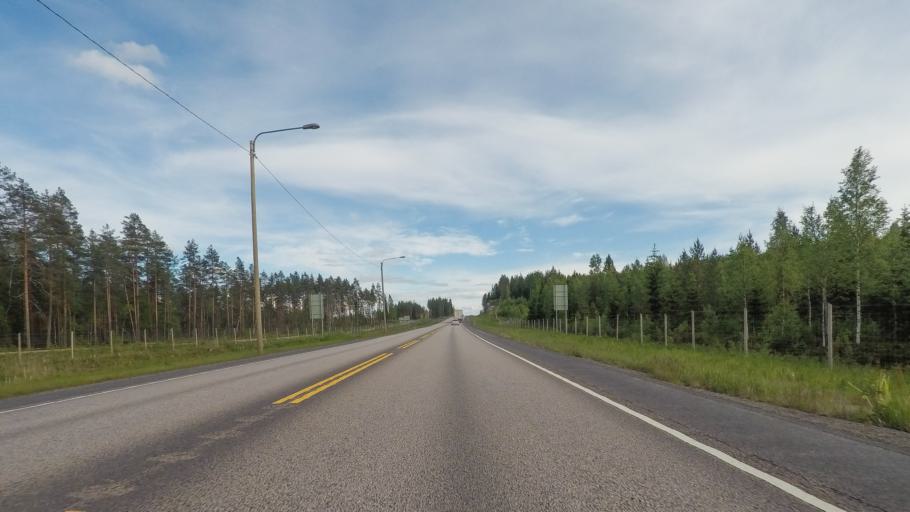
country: FI
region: Central Finland
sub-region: Jyvaeskylae
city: Toivakka
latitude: 62.0082
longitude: 26.0502
